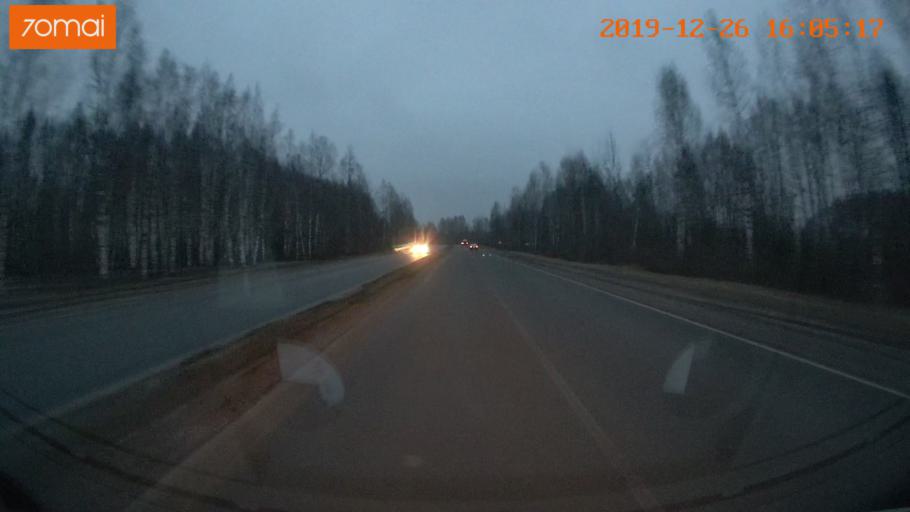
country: RU
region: Jaroslavl
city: Rybinsk
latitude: 58.0062
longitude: 38.8919
